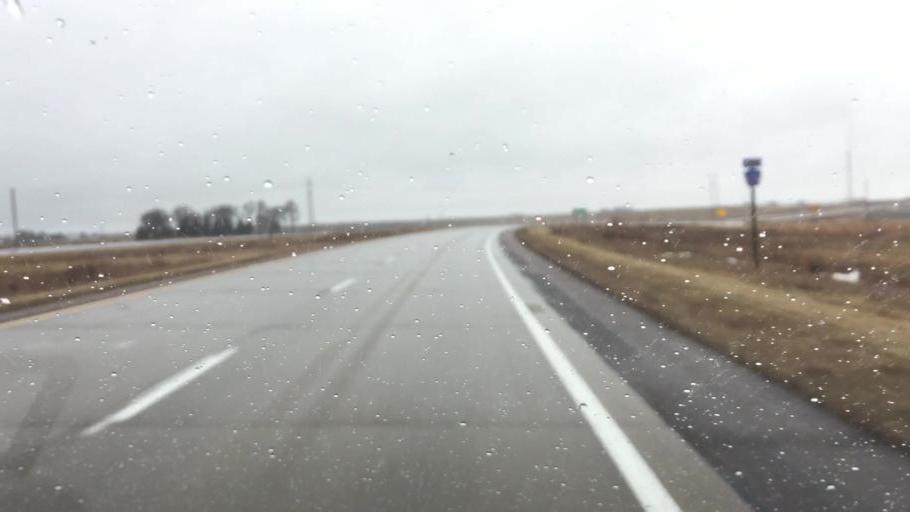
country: US
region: Iowa
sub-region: O'Brien County
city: Sheldon
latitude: 43.0647
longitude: -95.8987
